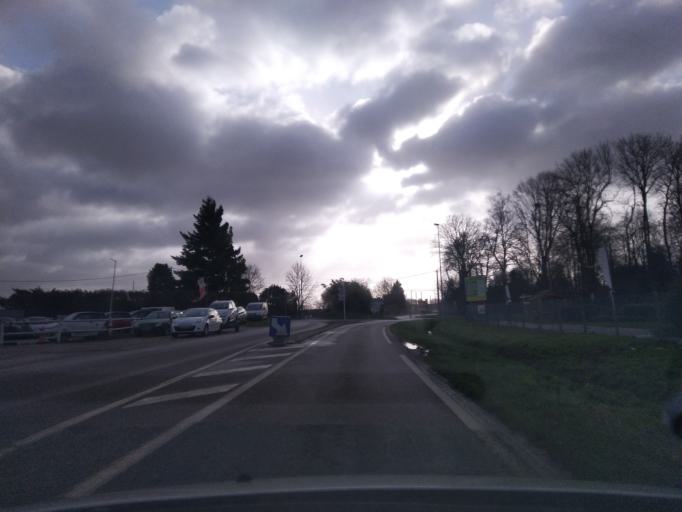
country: FR
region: Haute-Normandie
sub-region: Departement de la Seine-Maritime
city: Pissy-Poville
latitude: 49.5205
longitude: 0.9880
